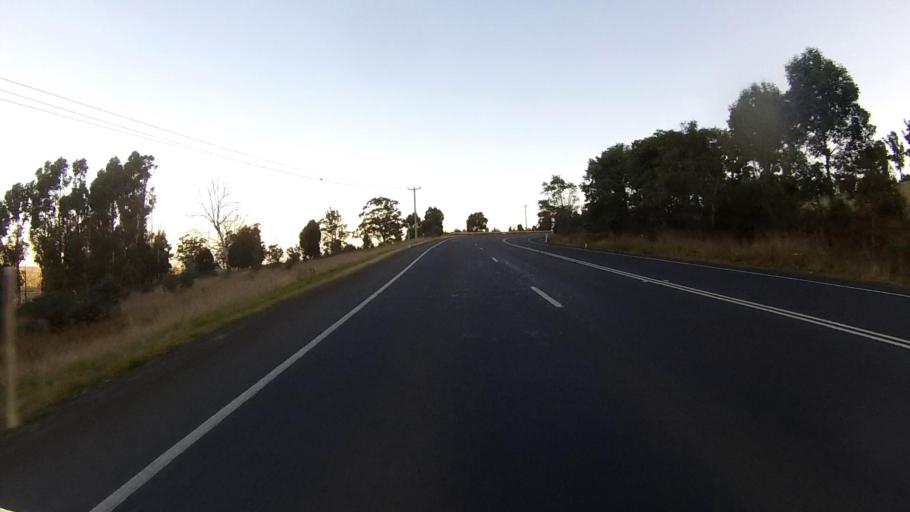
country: AU
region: Tasmania
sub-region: Sorell
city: Sorell
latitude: -42.8220
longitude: 147.7417
